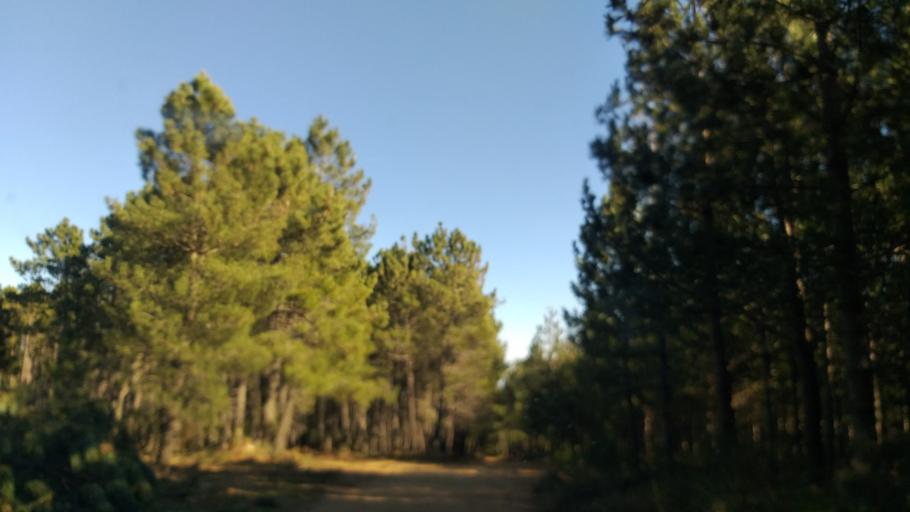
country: PT
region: Guarda
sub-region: Celorico da Beira
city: Celorico da Beira
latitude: 40.5146
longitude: -7.4074
